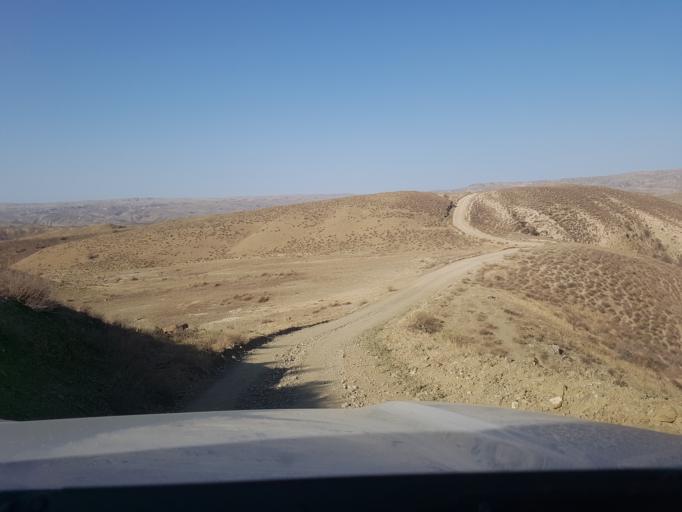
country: TM
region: Balkan
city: Magtymguly
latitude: 38.3010
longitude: 56.7937
